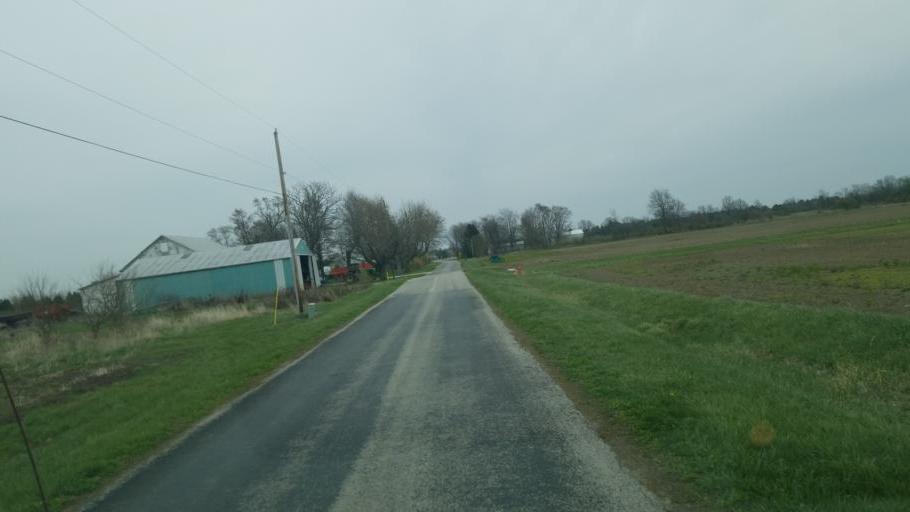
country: US
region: Ohio
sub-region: Wyandot County
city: Carey
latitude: 40.9750
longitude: -83.4978
